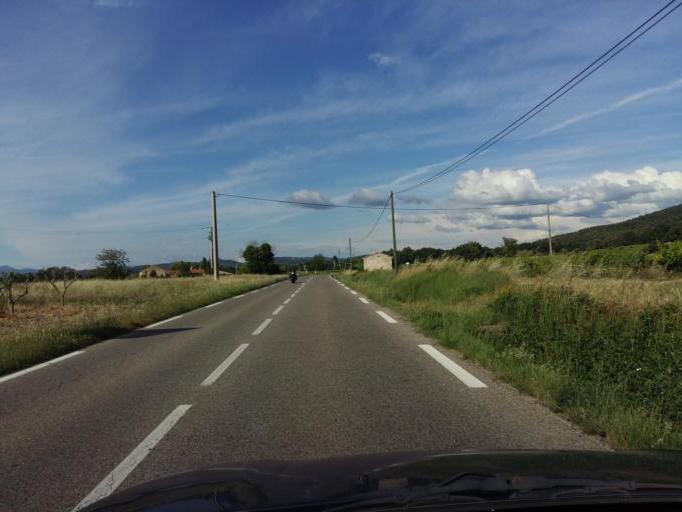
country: FR
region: Provence-Alpes-Cote d'Azur
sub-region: Departement du Vaucluse
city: Sablet
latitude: 44.2357
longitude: 5.0204
